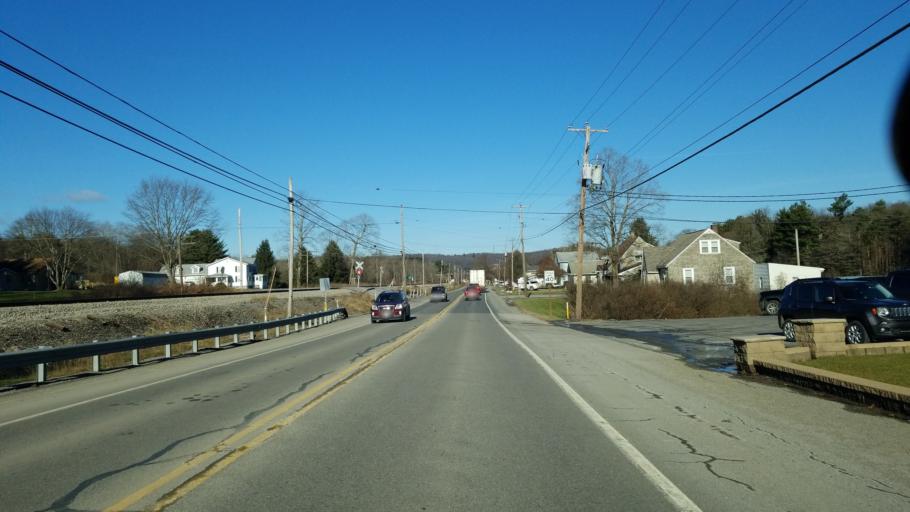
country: US
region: Pennsylvania
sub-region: Jefferson County
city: Brockway
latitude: 41.2312
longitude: -78.7825
